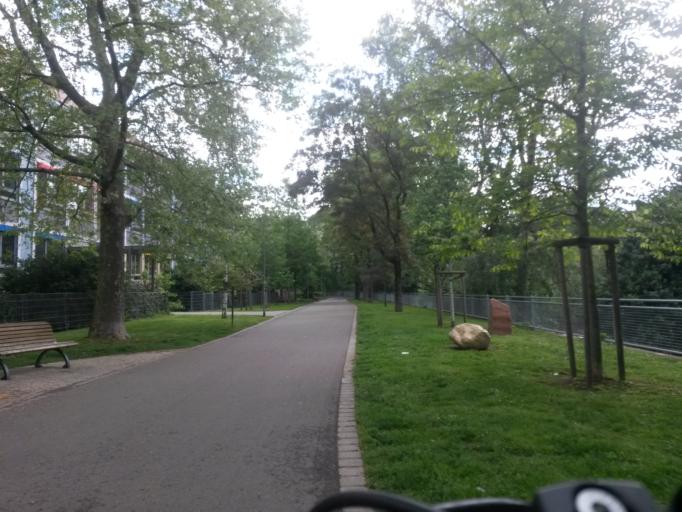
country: DE
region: Baden-Wuerttemberg
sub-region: Karlsruhe Region
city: Pforzheim
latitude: 48.8894
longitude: 8.7083
